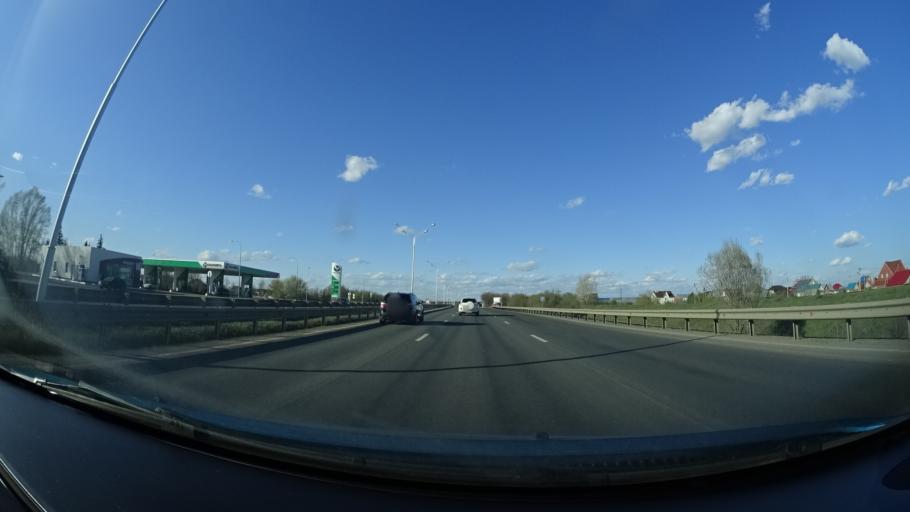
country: RU
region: Bashkortostan
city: Ufa
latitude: 54.6120
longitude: 55.9248
